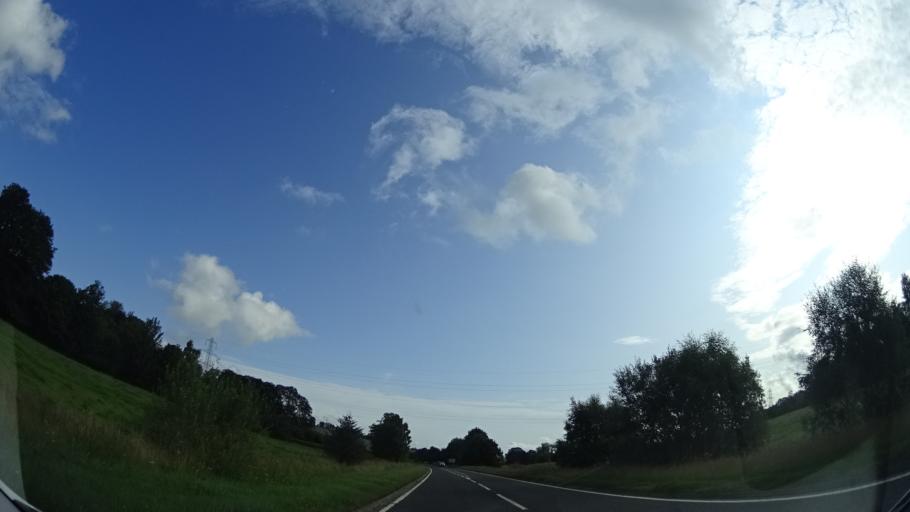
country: GB
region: Scotland
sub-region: Highland
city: Conon Bridge
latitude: 57.5739
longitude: -4.4522
